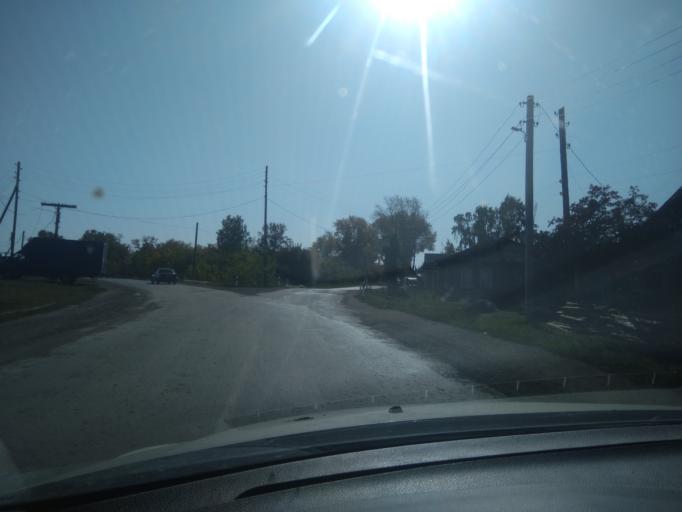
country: RU
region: Sverdlovsk
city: Pokrovskoye
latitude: 56.4660
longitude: 61.6152
